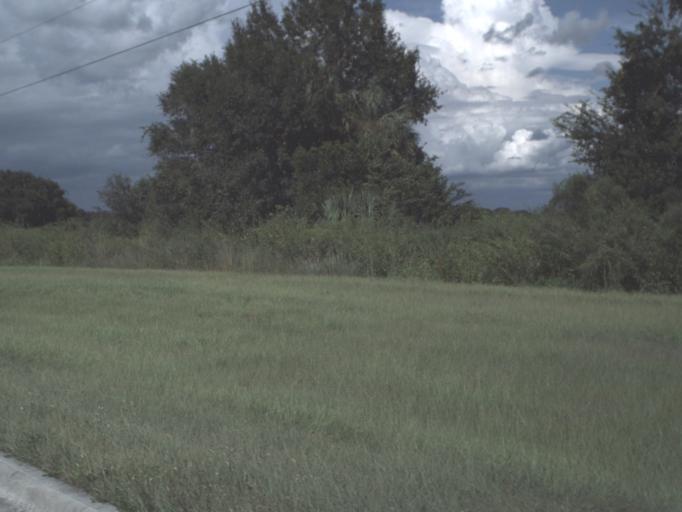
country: US
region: Florida
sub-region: Hardee County
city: Zolfo Springs
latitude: 27.4855
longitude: -81.7963
